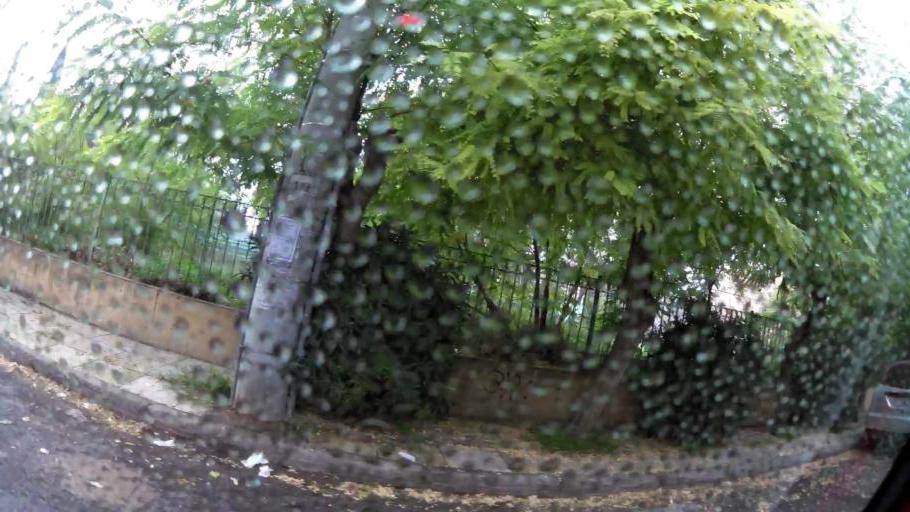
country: GR
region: Attica
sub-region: Nomarchia Athinas
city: Agioi Anargyroi
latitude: 38.0259
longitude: 23.7186
